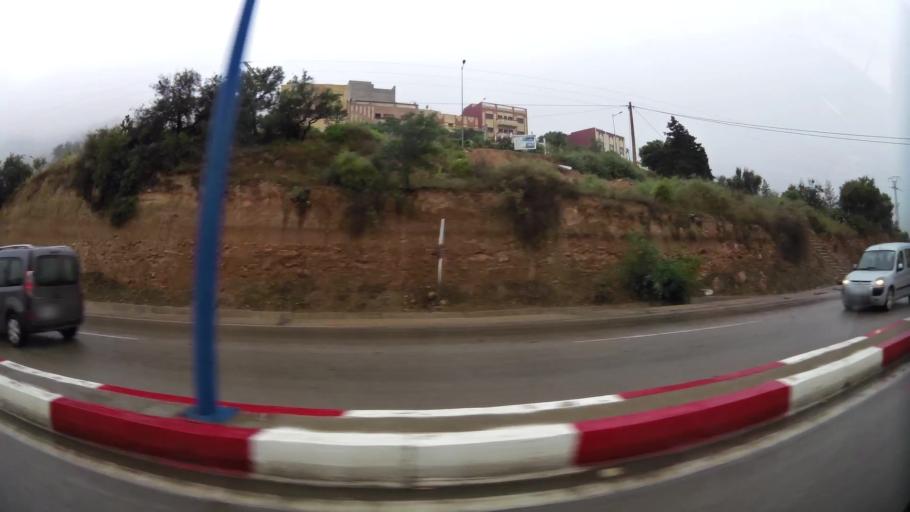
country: MA
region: Taza-Al Hoceima-Taounate
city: Tirhanimine
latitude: 35.2233
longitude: -3.9285
